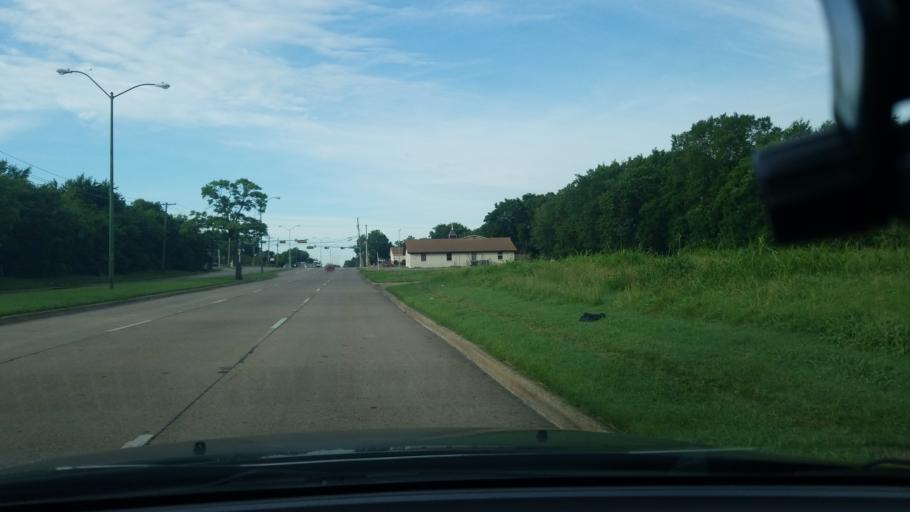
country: US
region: Texas
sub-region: Dallas County
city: Balch Springs
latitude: 32.7640
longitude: -96.6482
